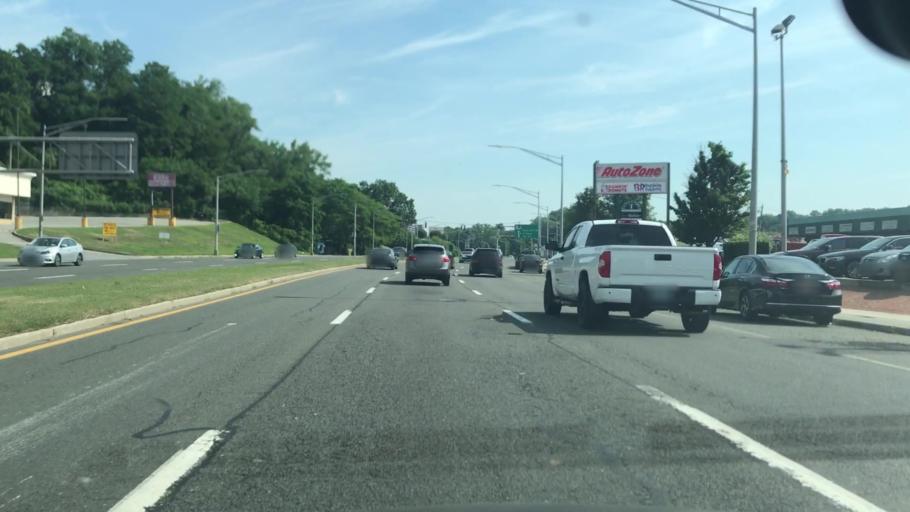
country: US
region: New York
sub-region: Westchester County
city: Greenville
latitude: 40.9747
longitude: -73.8333
